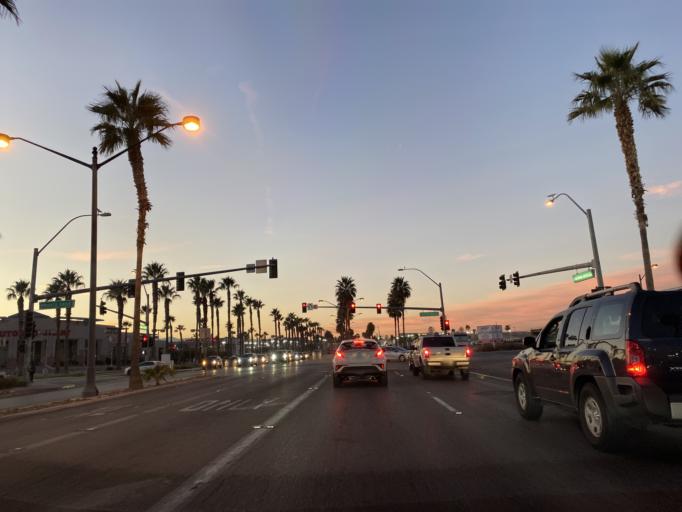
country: US
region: Nevada
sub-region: Clark County
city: Las Vegas
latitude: 36.2744
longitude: -115.2684
